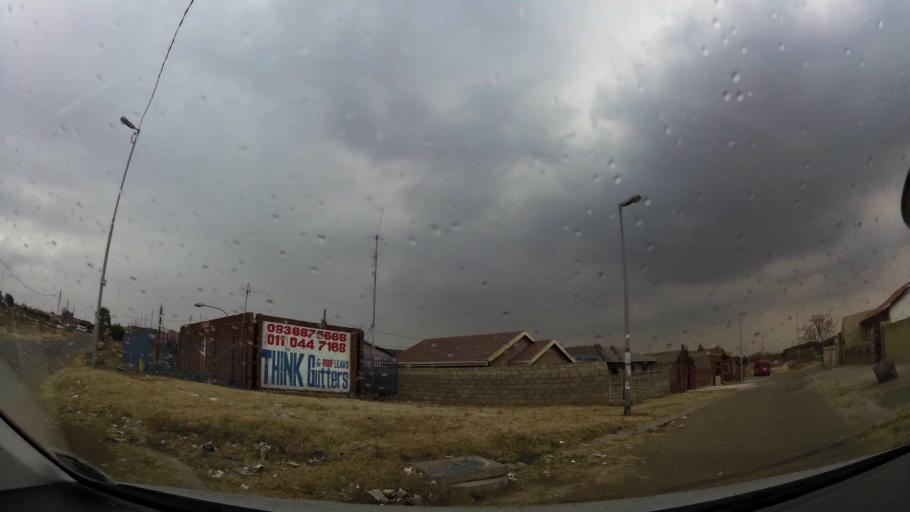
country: ZA
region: Gauteng
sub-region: City of Johannesburg Metropolitan Municipality
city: Soweto
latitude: -26.2590
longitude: 27.8718
